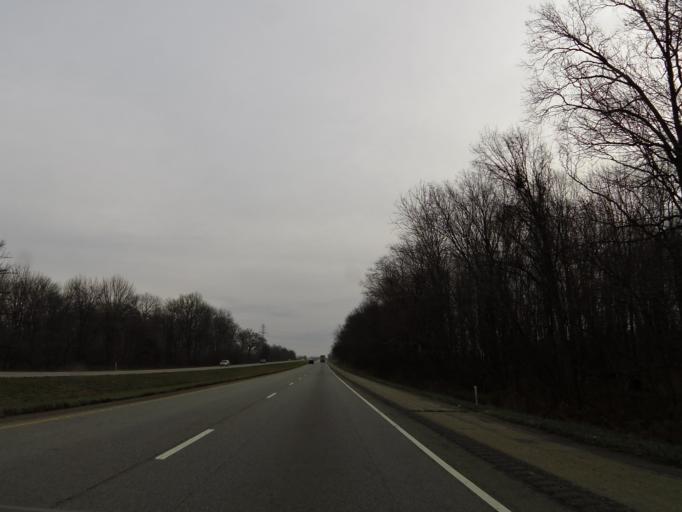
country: US
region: Indiana
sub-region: Fountain County
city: Covington
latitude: 40.1217
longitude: -87.3472
